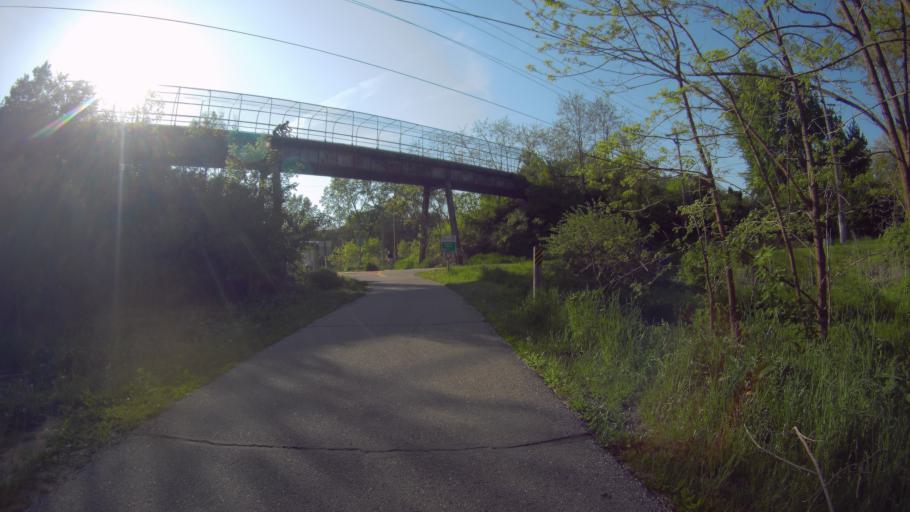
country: US
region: Wisconsin
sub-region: Dane County
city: Shorewood Hills
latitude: 43.0236
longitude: -89.4608
